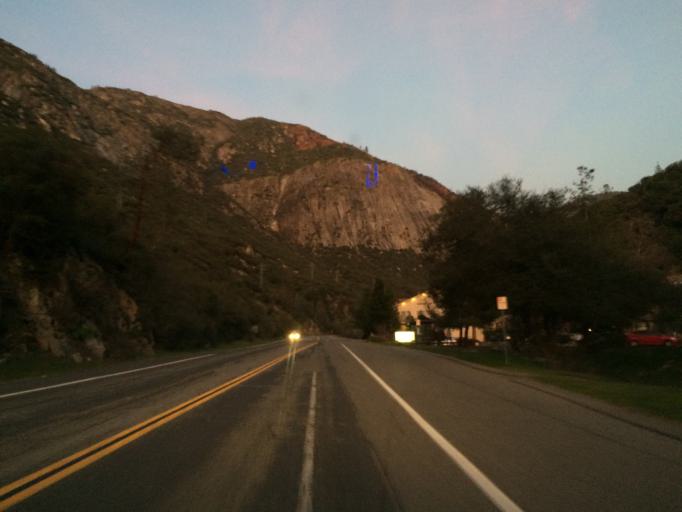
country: US
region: California
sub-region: Mariposa County
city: Yosemite Valley
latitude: 37.6783
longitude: -119.7666
